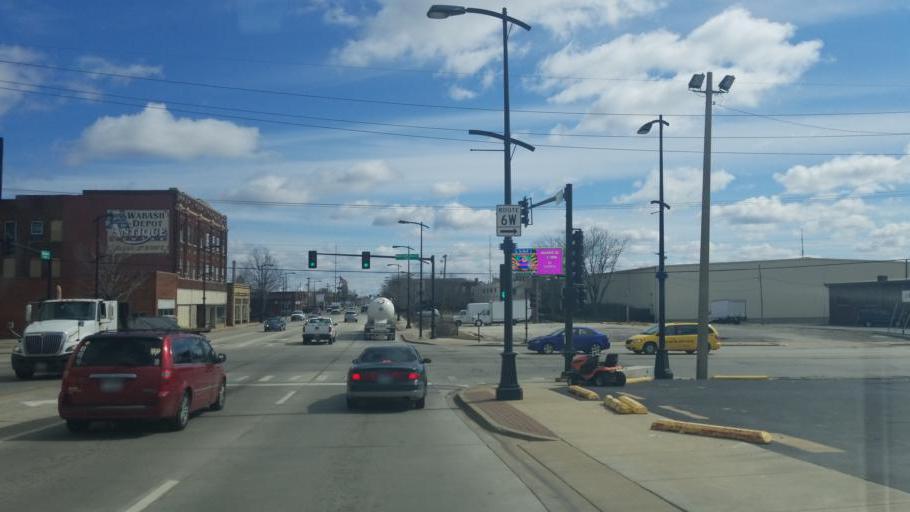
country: US
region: Illinois
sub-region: Macon County
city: Decatur
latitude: 39.8458
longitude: -88.9501
